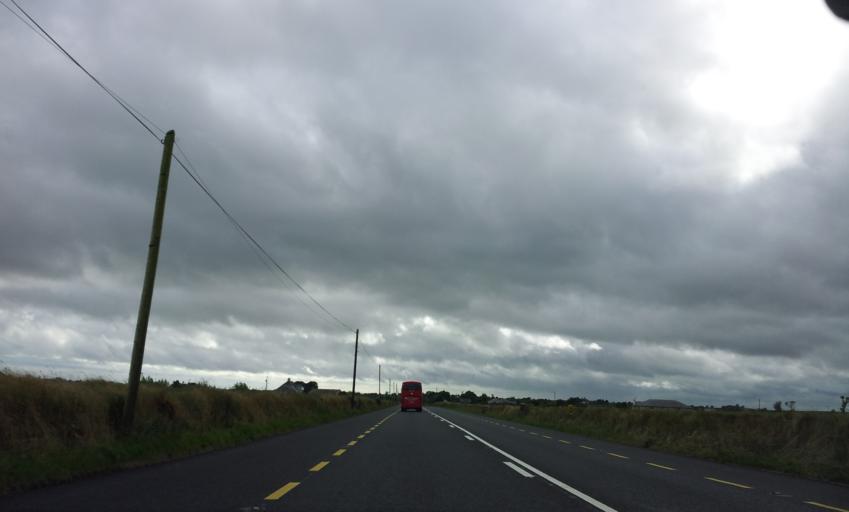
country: IE
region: Munster
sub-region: County Cork
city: Youghal
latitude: 51.9932
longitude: -7.7326
